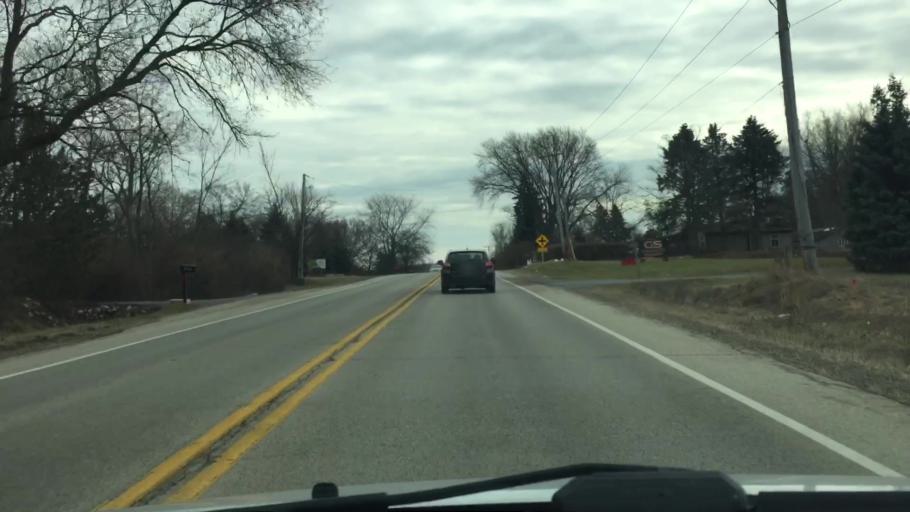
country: US
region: Illinois
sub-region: McHenry County
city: McCullom Lake
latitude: 42.3925
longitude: -88.2921
